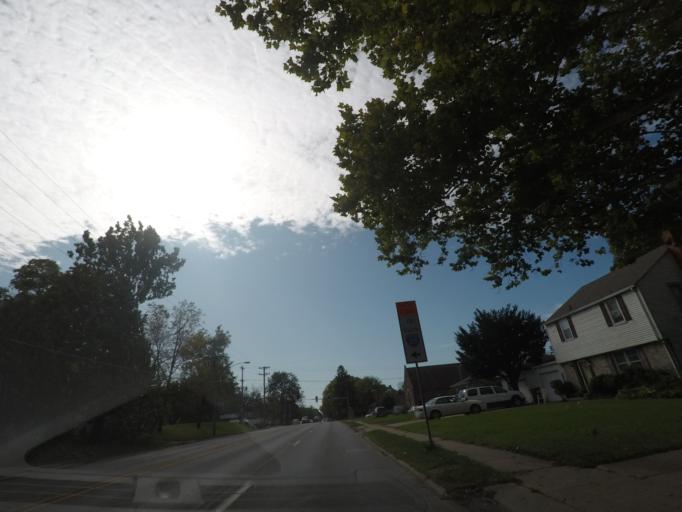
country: US
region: Iowa
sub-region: Story County
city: Ames
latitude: 42.0354
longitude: -93.6205
